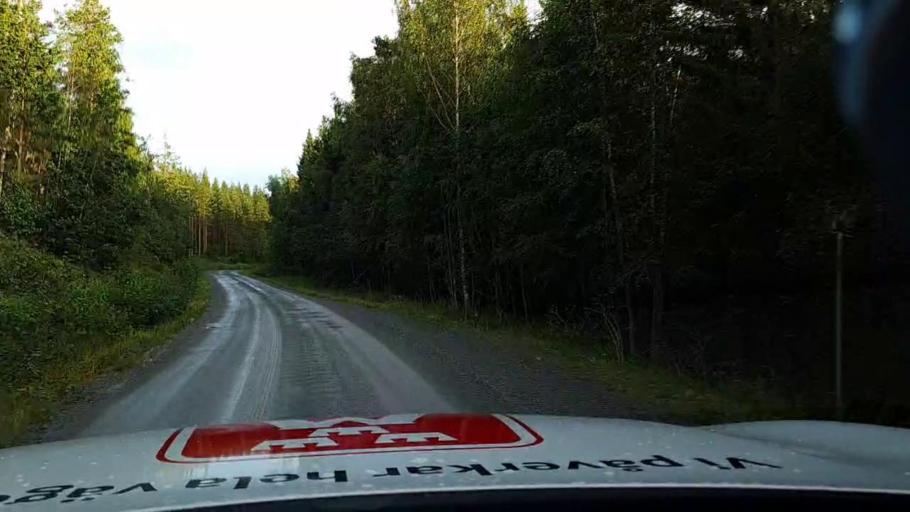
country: SE
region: Jaemtland
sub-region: Bergs Kommun
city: Hoverberg
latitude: 62.8621
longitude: 14.5309
